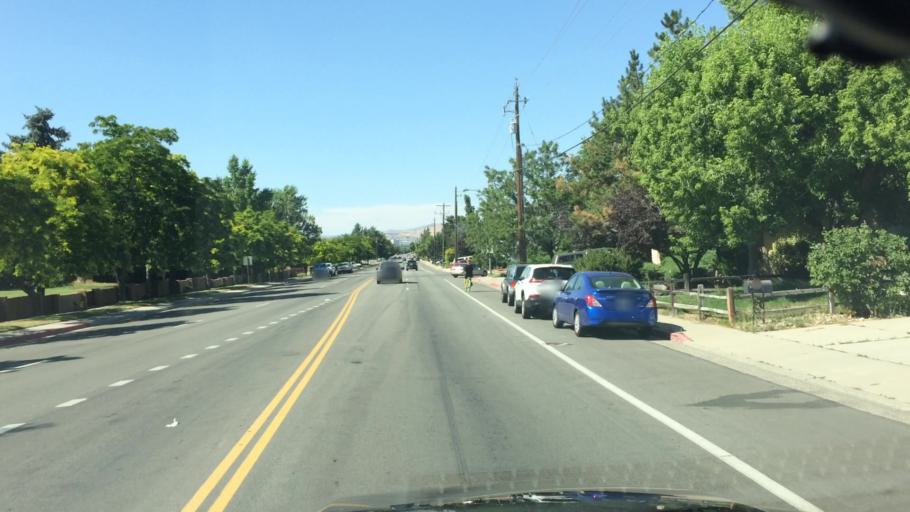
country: US
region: Nevada
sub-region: Washoe County
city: Reno
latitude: 39.4773
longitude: -119.8079
